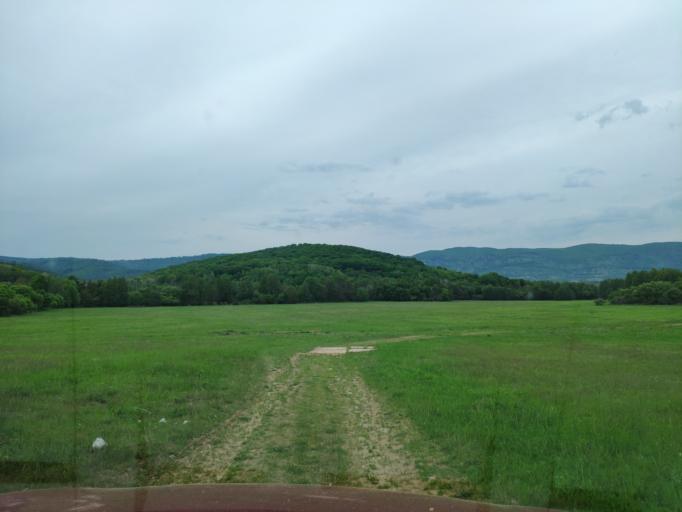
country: SK
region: Kosicky
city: Roznava
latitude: 48.5608
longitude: 20.6334
